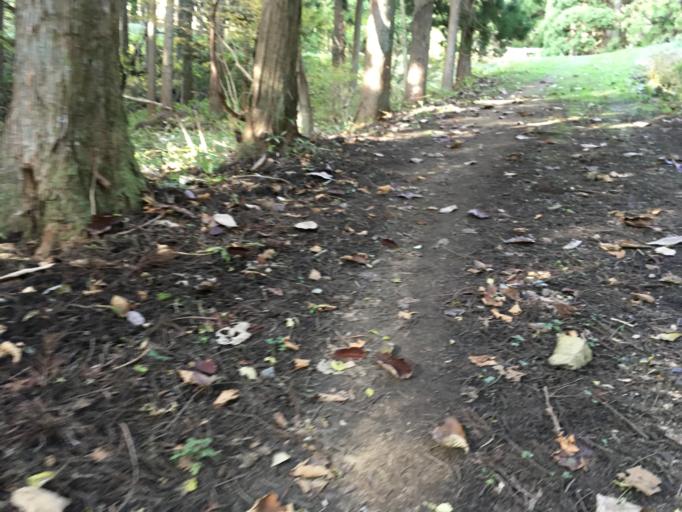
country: JP
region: Iwate
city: Ofunato
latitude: 38.9619
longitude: 141.4486
